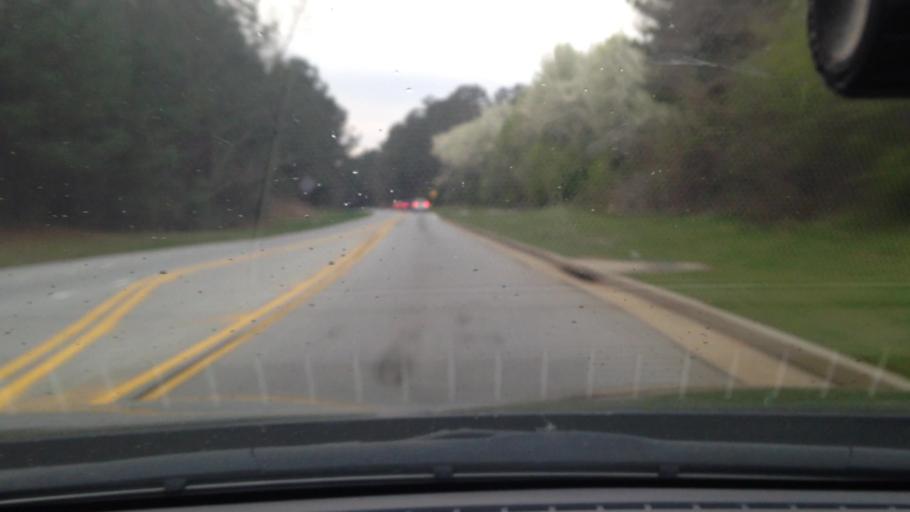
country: US
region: Georgia
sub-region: Coweta County
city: East Newnan
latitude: 33.3772
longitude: -84.7173
